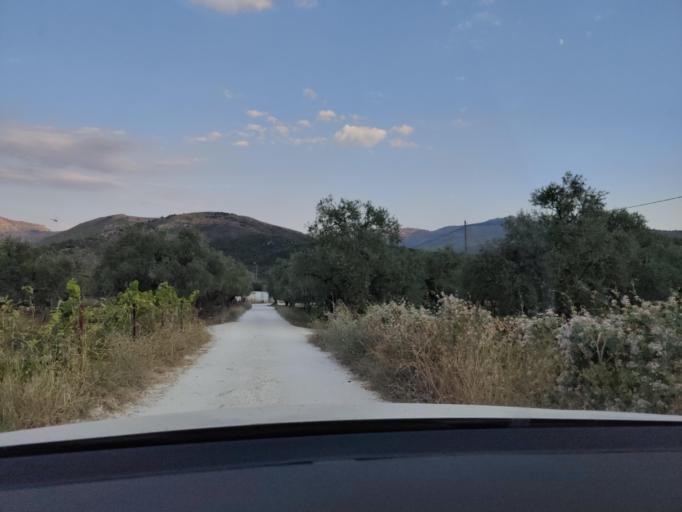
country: GR
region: East Macedonia and Thrace
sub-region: Nomos Kavalas
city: Prinos
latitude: 40.7500
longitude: 24.5736
